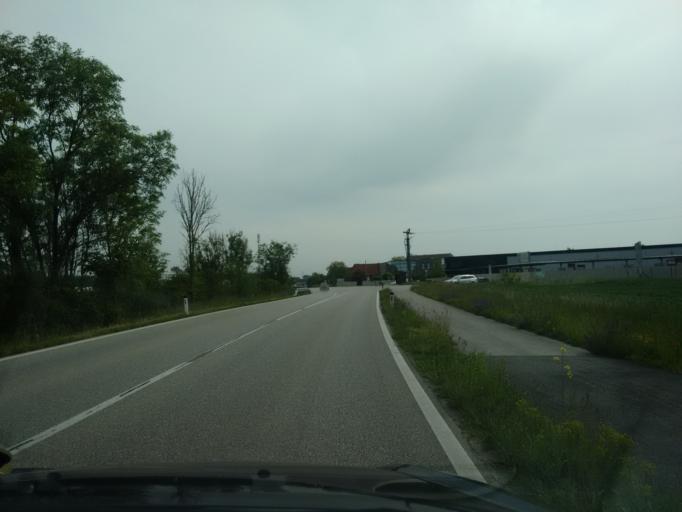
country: AT
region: Upper Austria
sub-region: Politischer Bezirk Linz-Land
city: Traun
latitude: 48.1935
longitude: 14.2106
